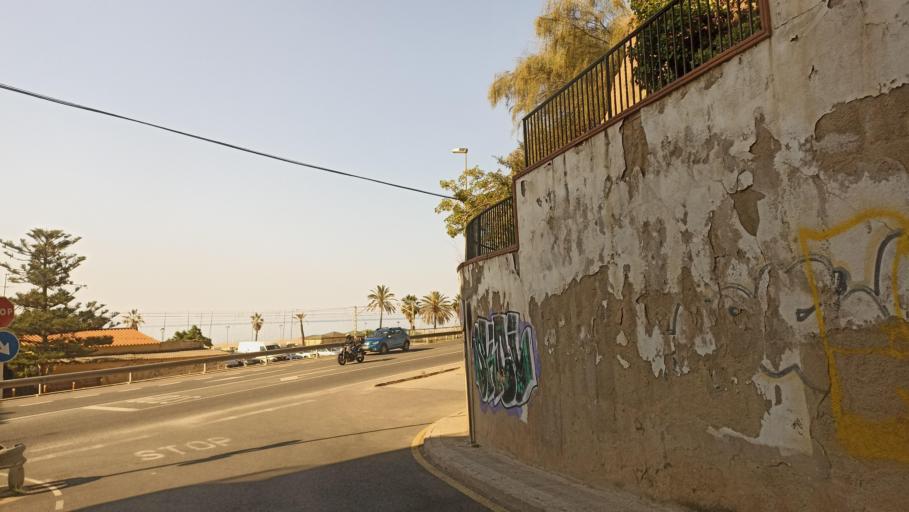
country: ES
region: Catalonia
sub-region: Provincia de Barcelona
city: Canet de Mar
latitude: 41.5865
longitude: 2.5790
